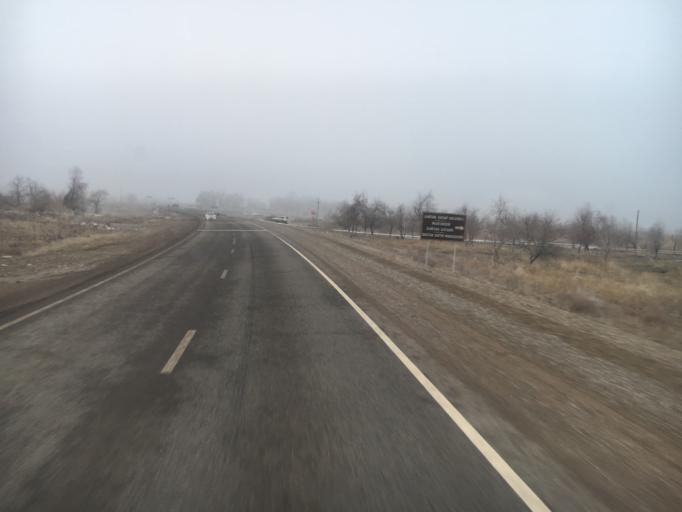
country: KZ
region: Zhambyl
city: Sarykemer
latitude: 43.0398
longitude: 71.5397
